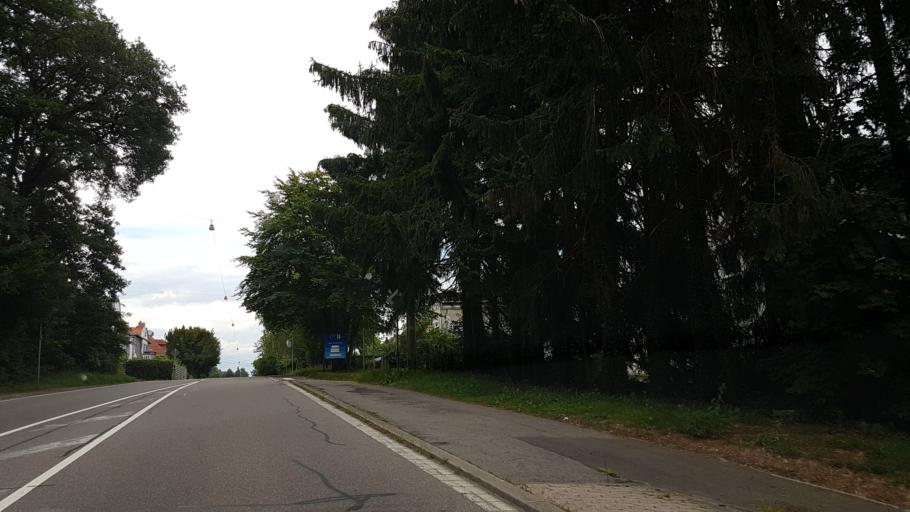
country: DE
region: Saarland
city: Friedrichsthal
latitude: 49.3271
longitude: 7.0862
